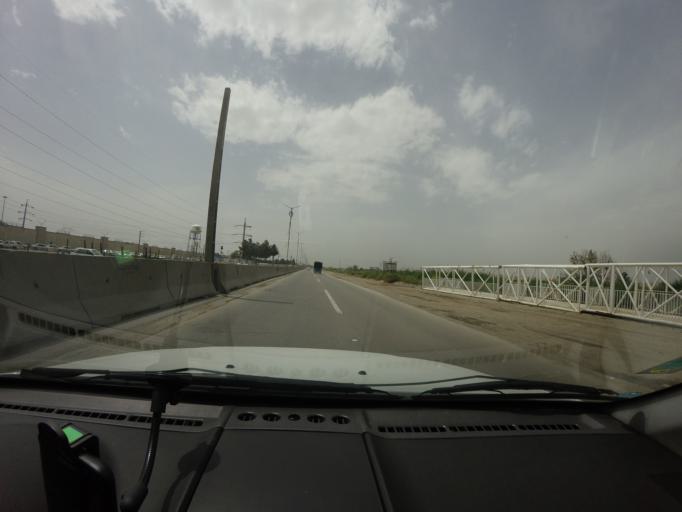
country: IR
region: Tehran
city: Eslamshahr
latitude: 35.5120
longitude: 51.2520
